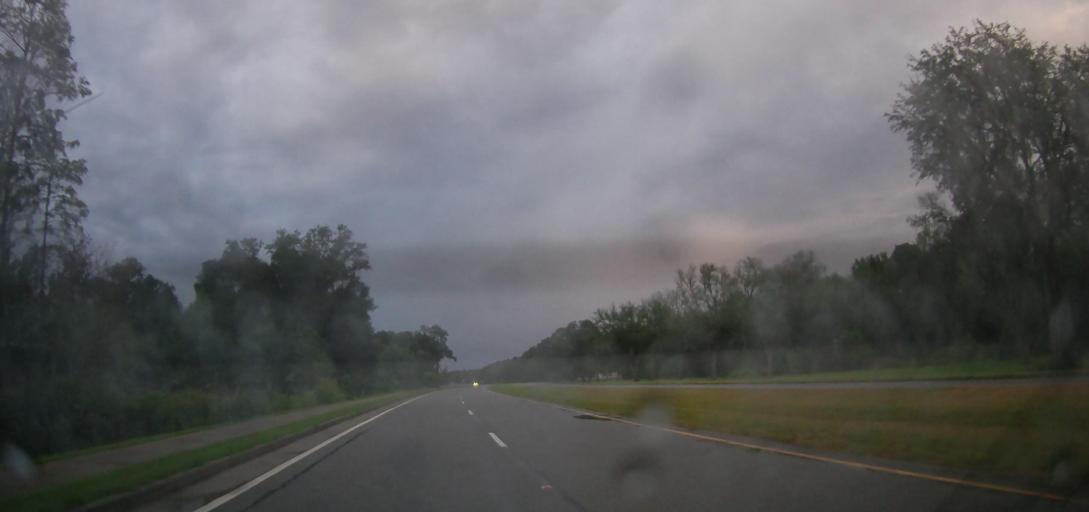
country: US
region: Georgia
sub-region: Lanier County
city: Lakeland
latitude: 30.9407
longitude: -82.9972
